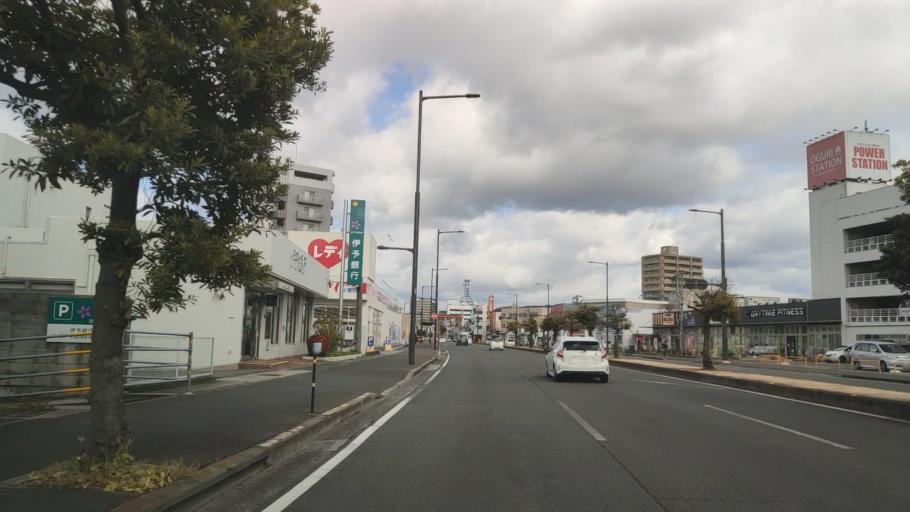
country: JP
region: Ehime
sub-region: Shikoku-chuo Shi
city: Matsuyama
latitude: 33.8265
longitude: 132.7587
